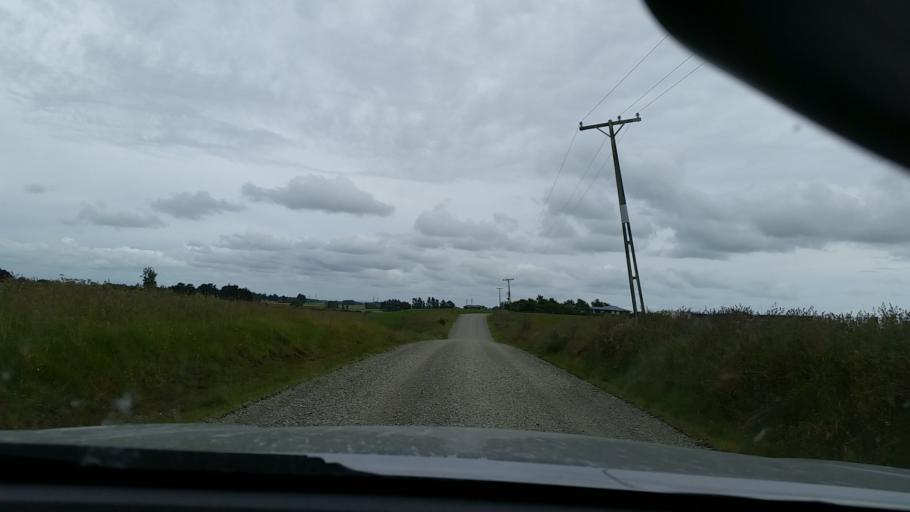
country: NZ
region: Southland
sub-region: Southland District
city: Winton
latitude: -46.2180
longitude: 168.2633
